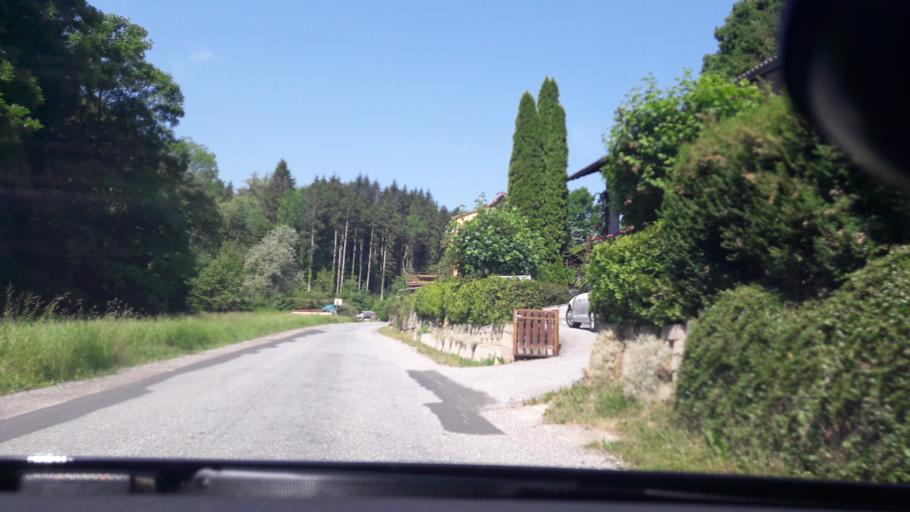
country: AT
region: Styria
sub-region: Politischer Bezirk Voitsberg
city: Sodingberg
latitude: 47.1083
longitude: 15.1693
